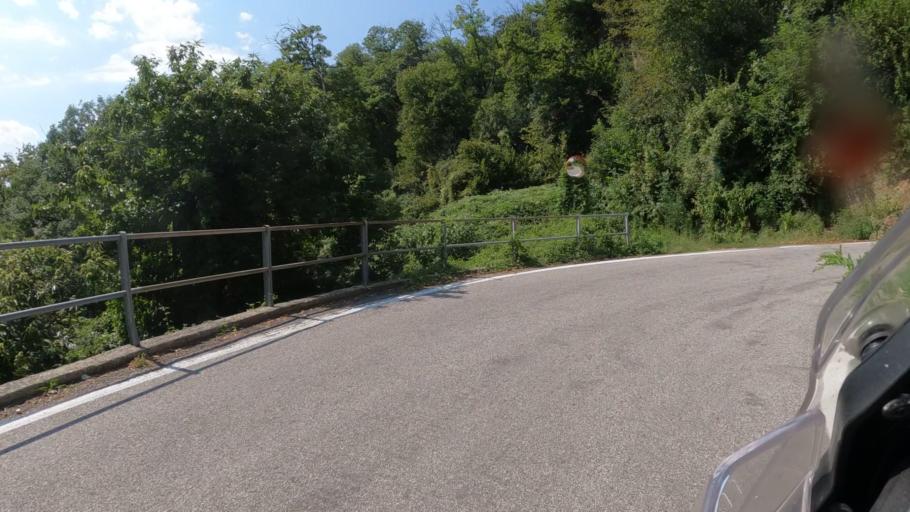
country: IT
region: Lombardy
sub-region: Provincia di Varese
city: Maccagno
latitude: 46.0476
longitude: 8.7455
